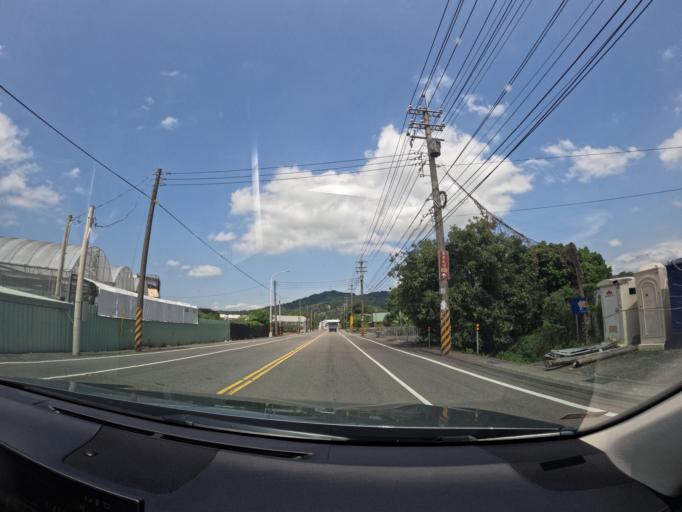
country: TW
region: Taiwan
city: Fengyuan
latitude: 24.2695
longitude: 120.8240
